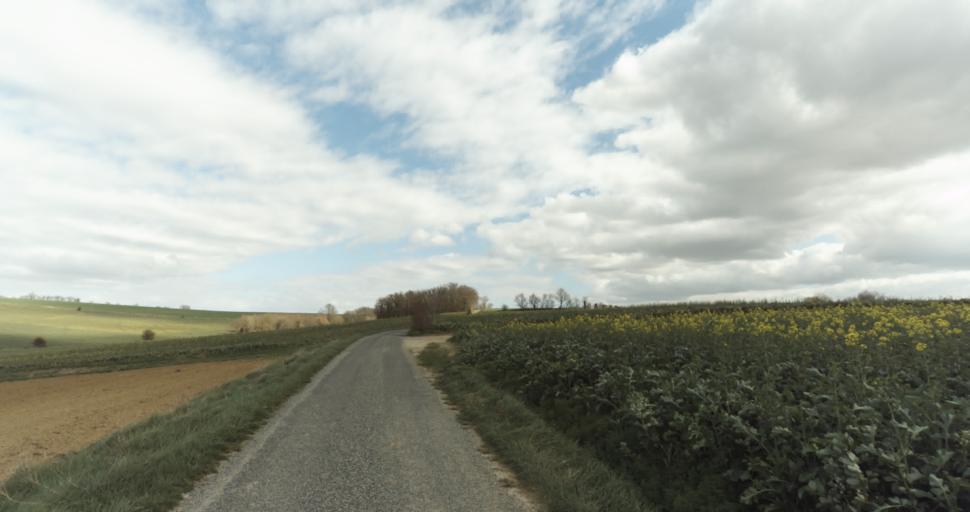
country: FR
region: Midi-Pyrenees
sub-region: Departement de la Haute-Garonne
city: Auterive
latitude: 43.3856
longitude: 1.4783
